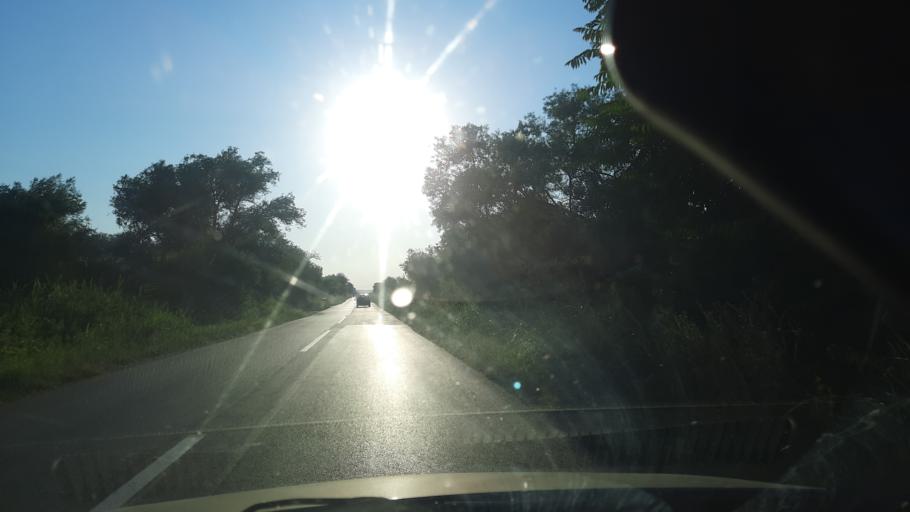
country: RS
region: Central Serbia
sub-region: Branicevski Okrug
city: Malo Crnice
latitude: 44.5761
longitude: 21.3433
